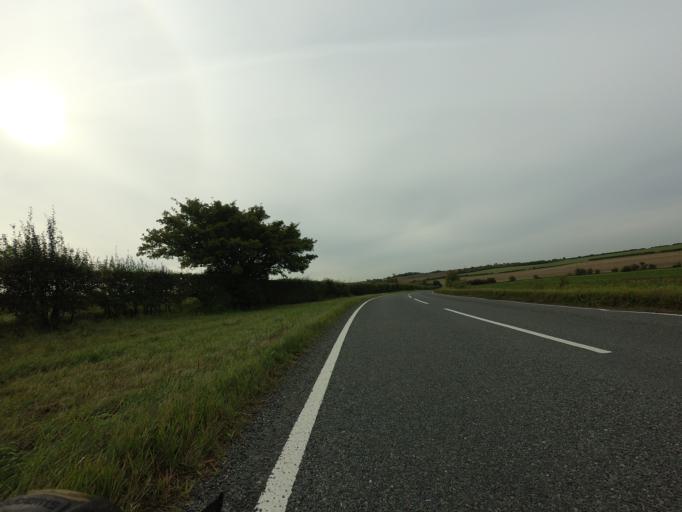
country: GB
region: England
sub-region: Cambridgeshire
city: Melbourn
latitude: 52.0440
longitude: 0.0450
